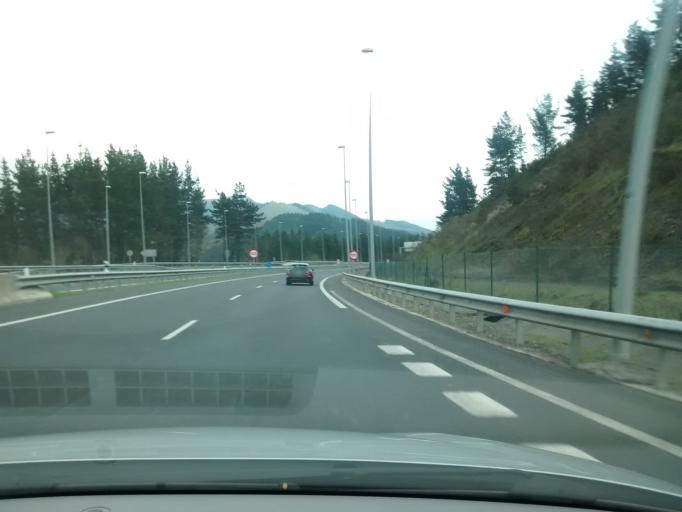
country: ES
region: Basque Country
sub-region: Bizkaia
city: Gordexola
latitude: 43.1975
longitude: -3.0750
